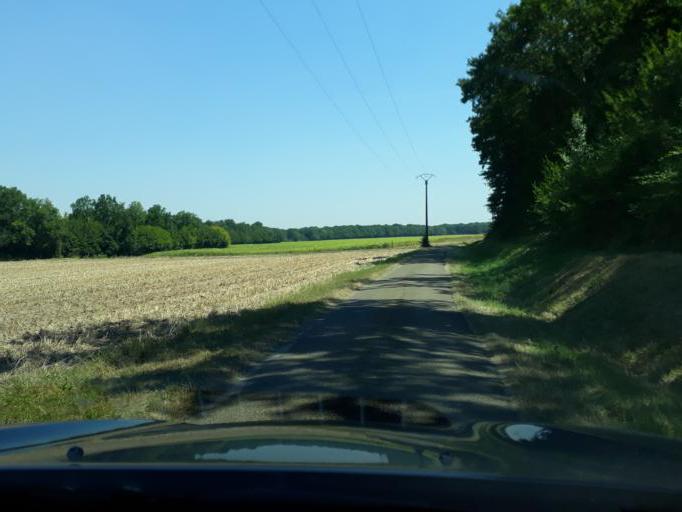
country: FR
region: Centre
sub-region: Departement du Loiret
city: Saran
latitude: 47.9899
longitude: 1.8999
